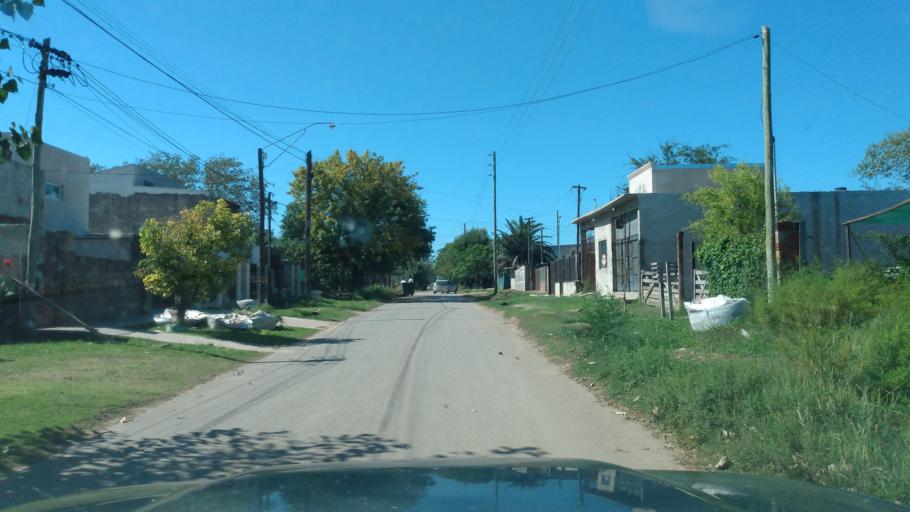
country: AR
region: Buenos Aires
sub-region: Partido de Lujan
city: Lujan
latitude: -34.5813
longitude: -59.1278
